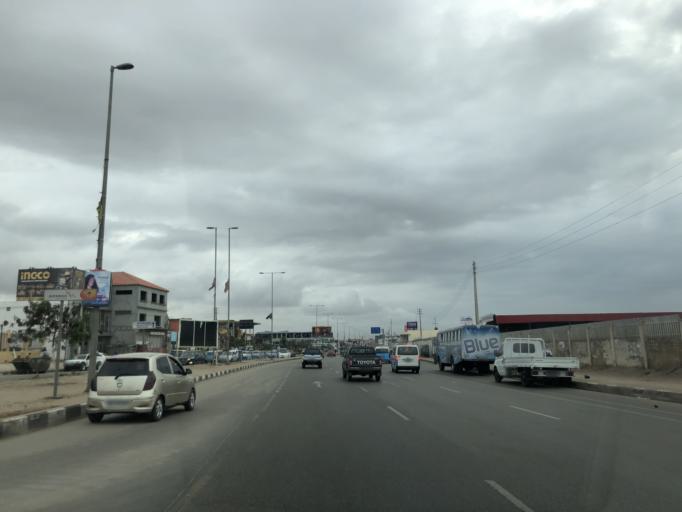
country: AO
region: Luanda
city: Luanda
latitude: -8.8837
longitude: 13.2074
